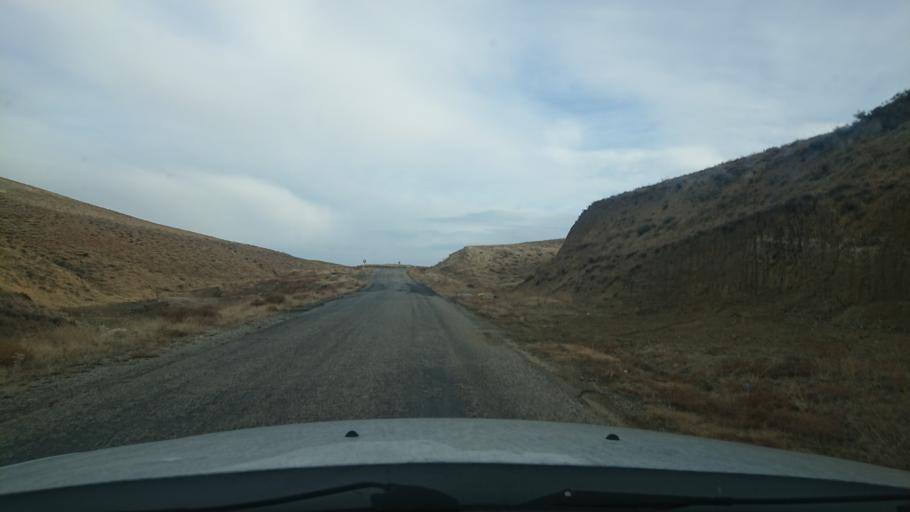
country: TR
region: Aksaray
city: Acipinar
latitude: 38.6312
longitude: 33.8001
